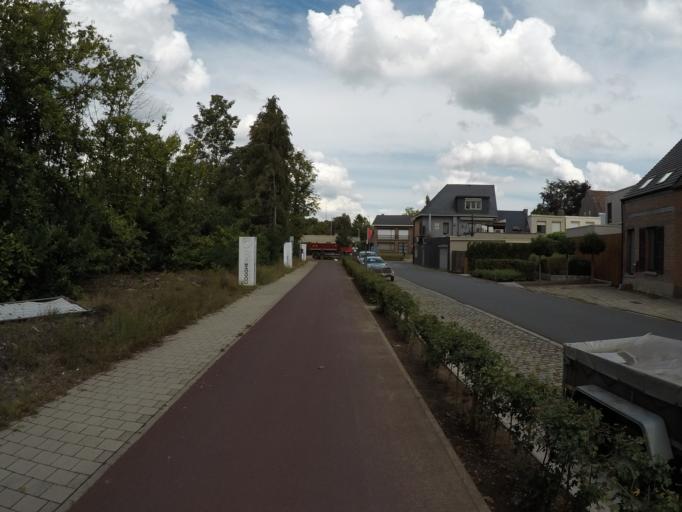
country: BE
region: Flanders
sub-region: Provincie Antwerpen
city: Wommelgem
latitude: 51.1965
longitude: 4.5282
